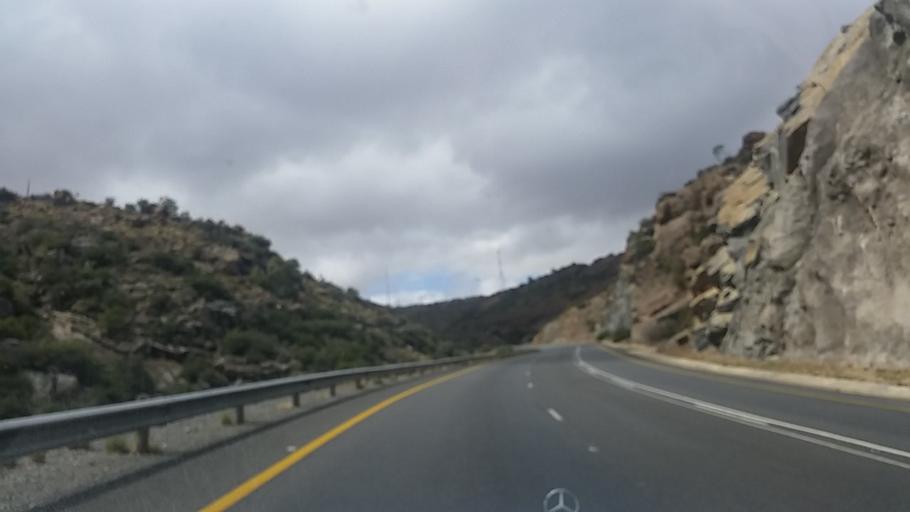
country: ZA
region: Eastern Cape
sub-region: Cacadu District Municipality
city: Graaff-Reinet
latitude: -31.9682
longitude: 24.7186
